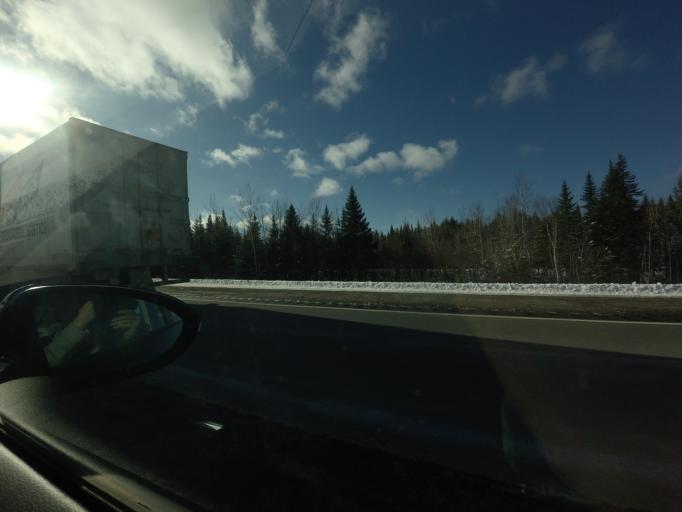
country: CA
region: New Brunswick
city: Fredericton
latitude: 45.8800
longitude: -66.6362
